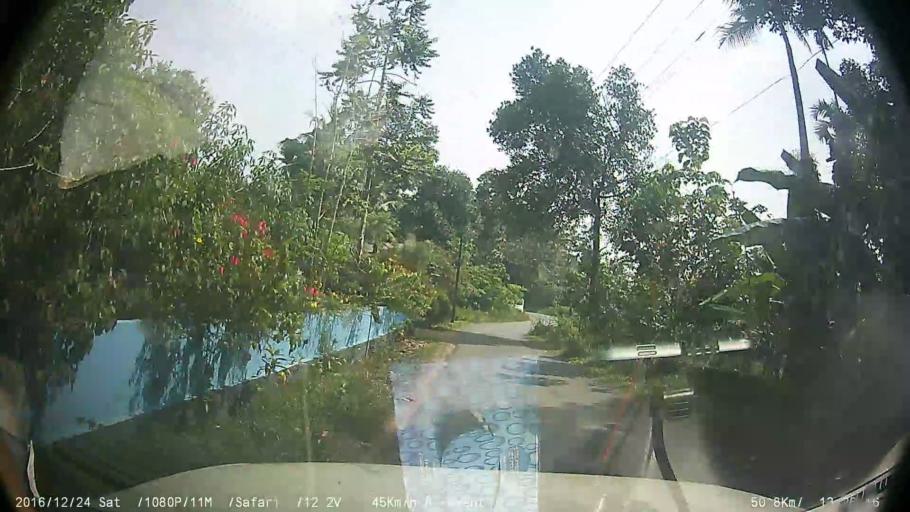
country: IN
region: Kerala
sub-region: Kottayam
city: Palackattumala
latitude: 9.8655
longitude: 76.6860
